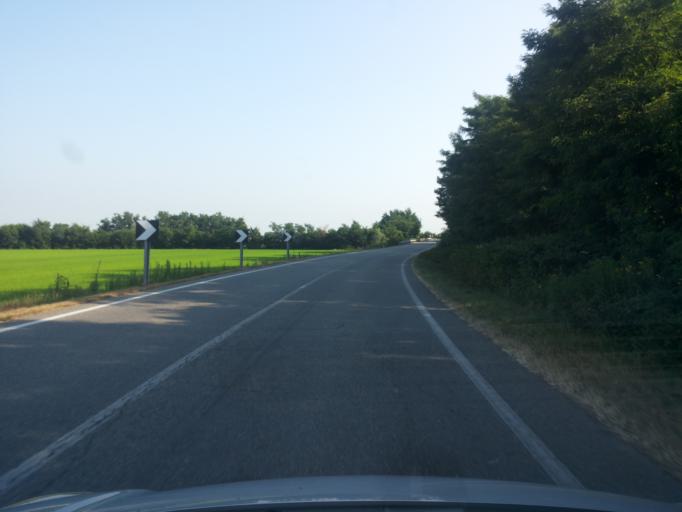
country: IT
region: Piedmont
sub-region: Provincia di Biella
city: Gifflenga
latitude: 45.4752
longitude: 8.2189
